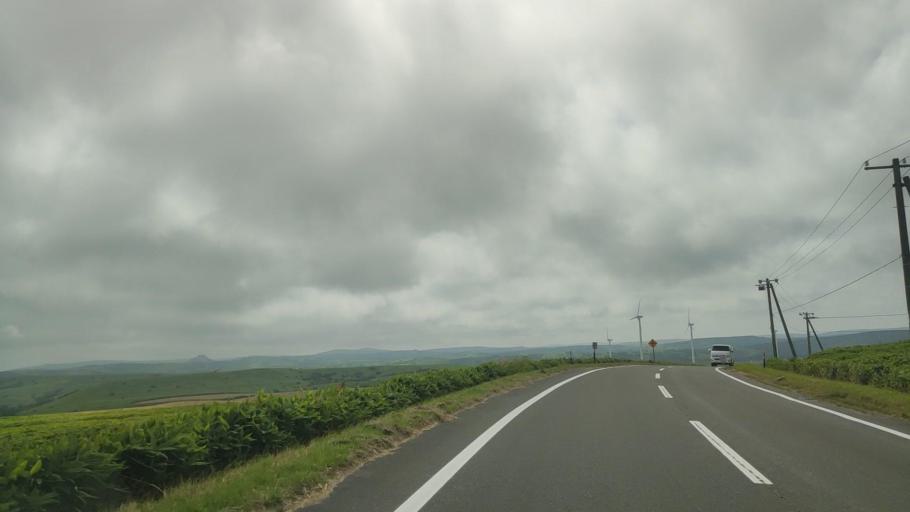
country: JP
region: Hokkaido
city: Makubetsu
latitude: 45.4876
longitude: 141.9383
